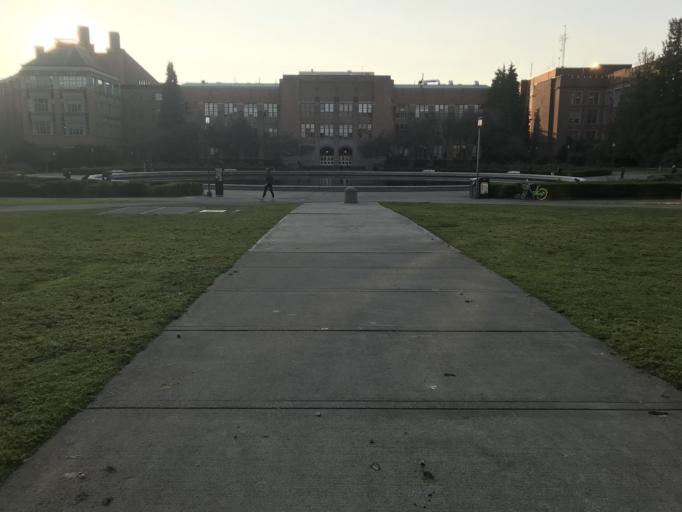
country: US
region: Washington
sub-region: King County
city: Seattle
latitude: 47.6541
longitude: -122.3069
